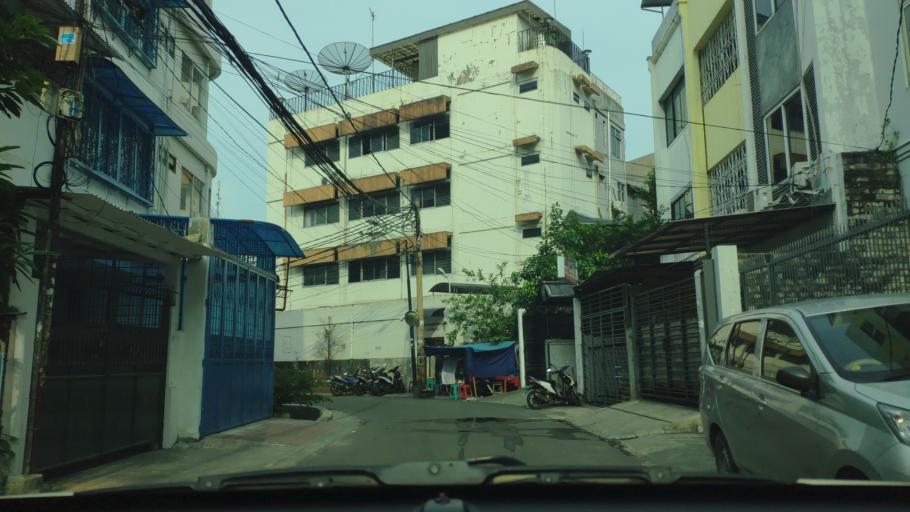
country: ID
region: Jakarta Raya
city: Jakarta
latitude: -6.1605
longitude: 106.8218
